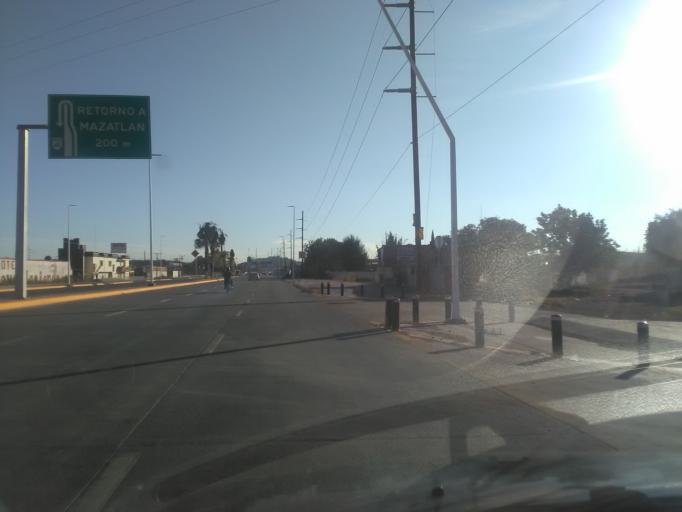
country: MX
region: Durango
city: Victoria de Durango
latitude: 23.9971
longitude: -104.7020
